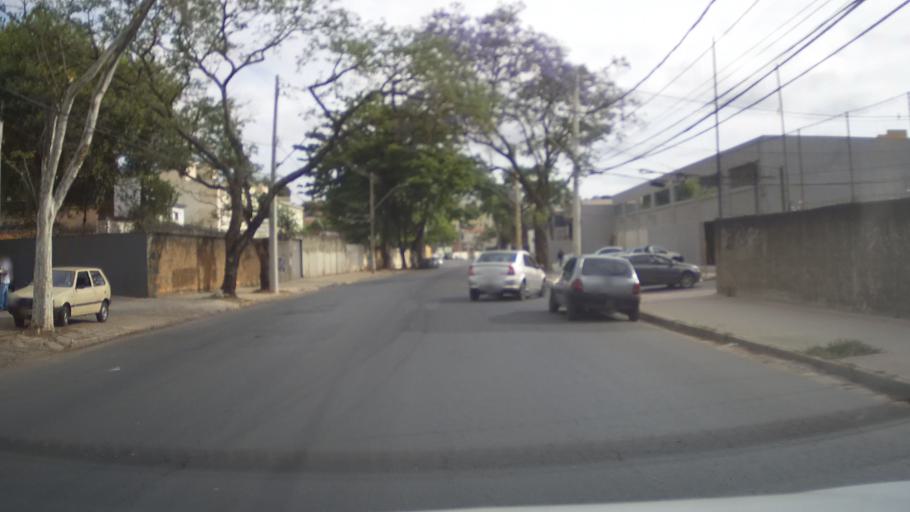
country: BR
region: Minas Gerais
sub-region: Belo Horizonte
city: Belo Horizonte
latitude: -19.8274
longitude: -43.9615
